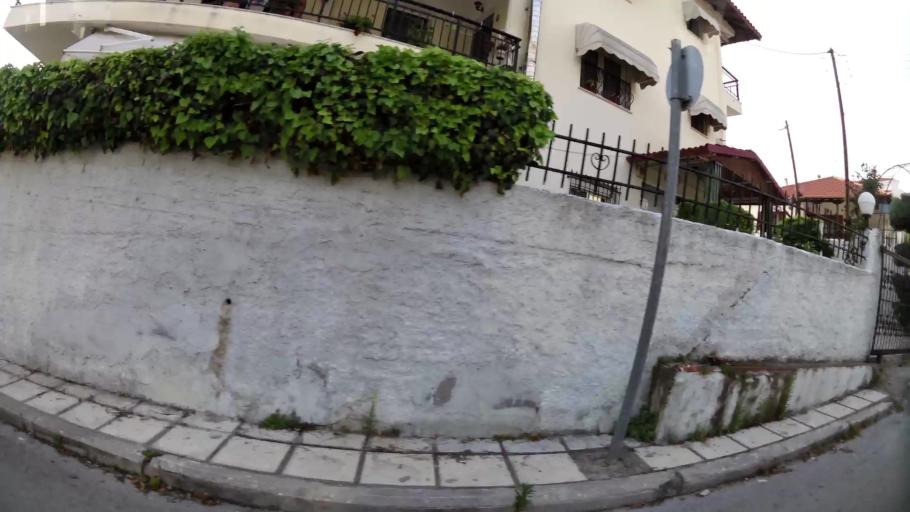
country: GR
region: Central Macedonia
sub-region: Nomos Thessalonikis
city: Oraiokastro
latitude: 40.7233
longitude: 22.9078
